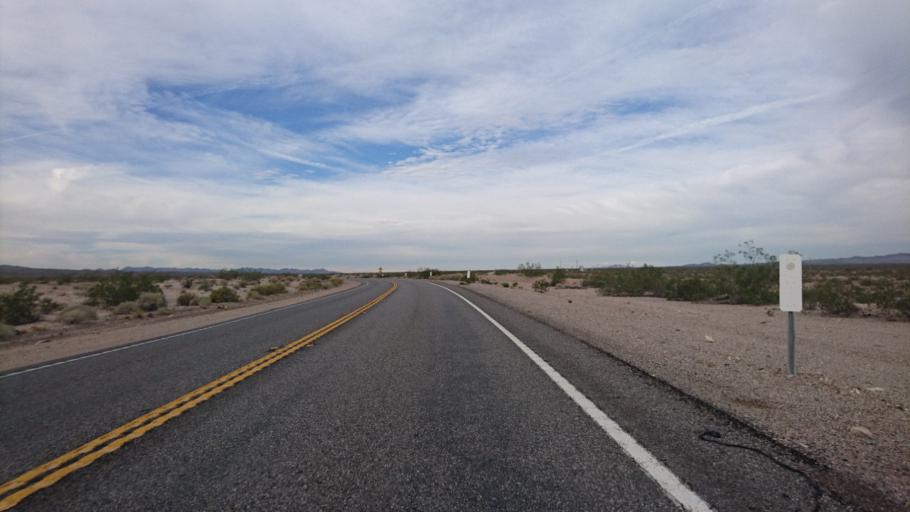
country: US
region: Arizona
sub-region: Mohave County
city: Willow Valley
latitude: 34.9410
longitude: -114.8163
